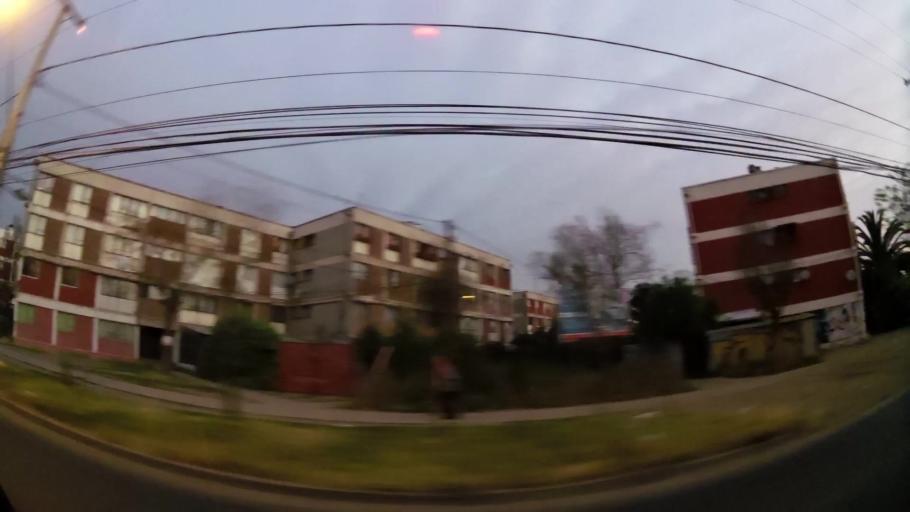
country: CL
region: Santiago Metropolitan
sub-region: Provincia de Santiago
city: Lo Prado
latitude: -33.4696
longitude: -70.7157
